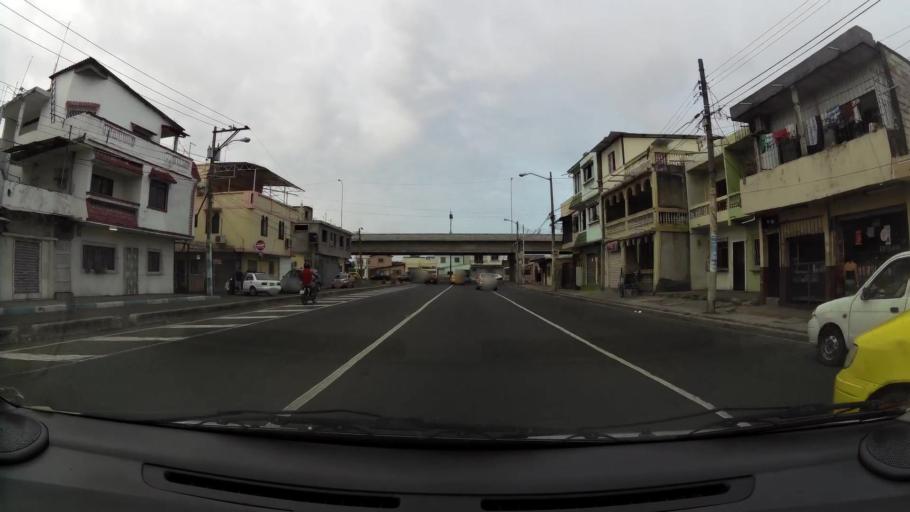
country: EC
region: Guayas
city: Guayaquil
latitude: -2.2216
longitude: -79.9001
